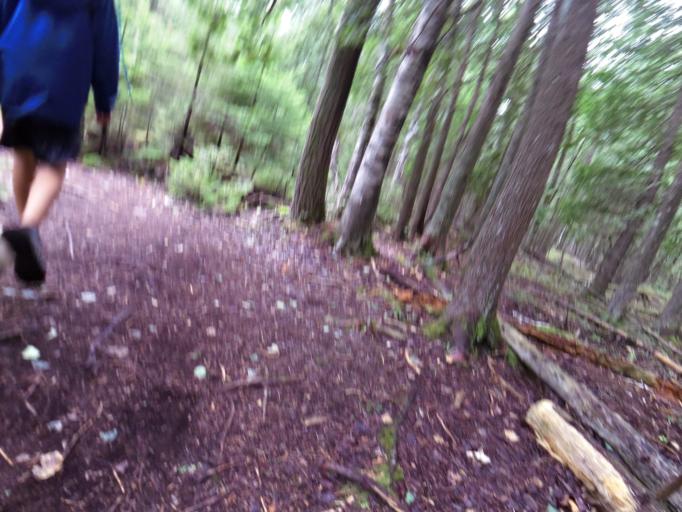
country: CA
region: Ontario
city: Tobermory
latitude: 45.2611
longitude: -81.6493
